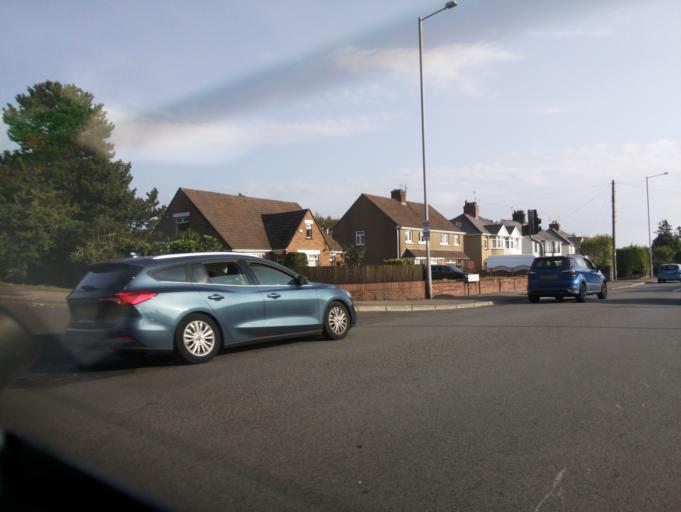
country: GB
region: Wales
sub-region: Torfaen County Borough
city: Cwmbran
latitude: 51.6698
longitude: -3.0180
